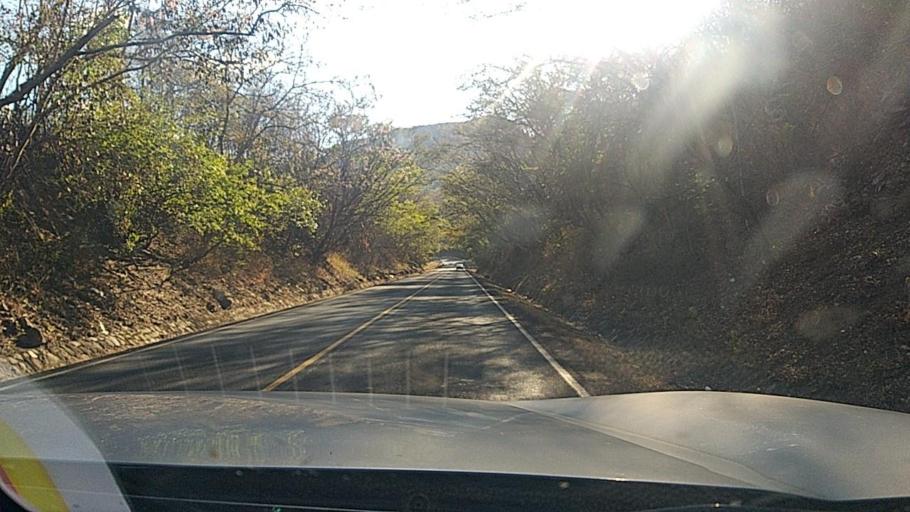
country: NI
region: Esteli
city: Condega
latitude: 13.2784
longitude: -86.3496
